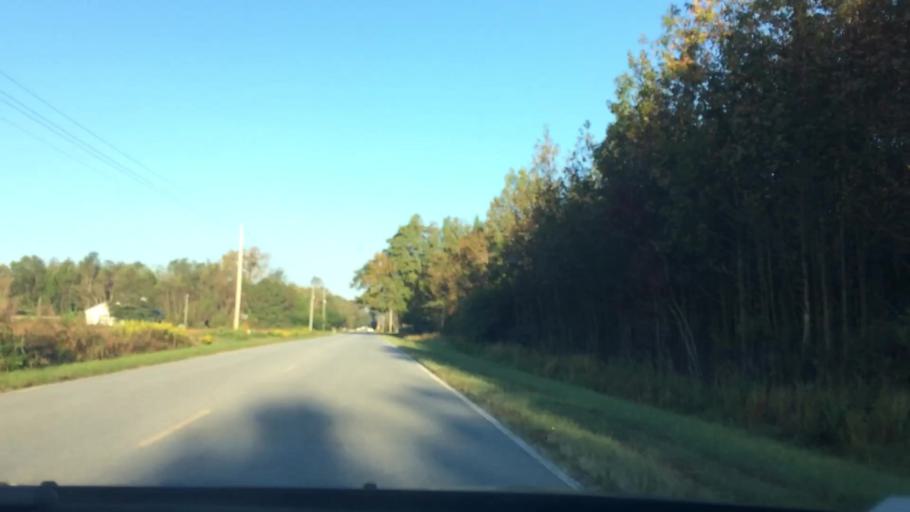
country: US
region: North Carolina
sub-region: Pitt County
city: Grifton
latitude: 35.4033
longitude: -77.4163
